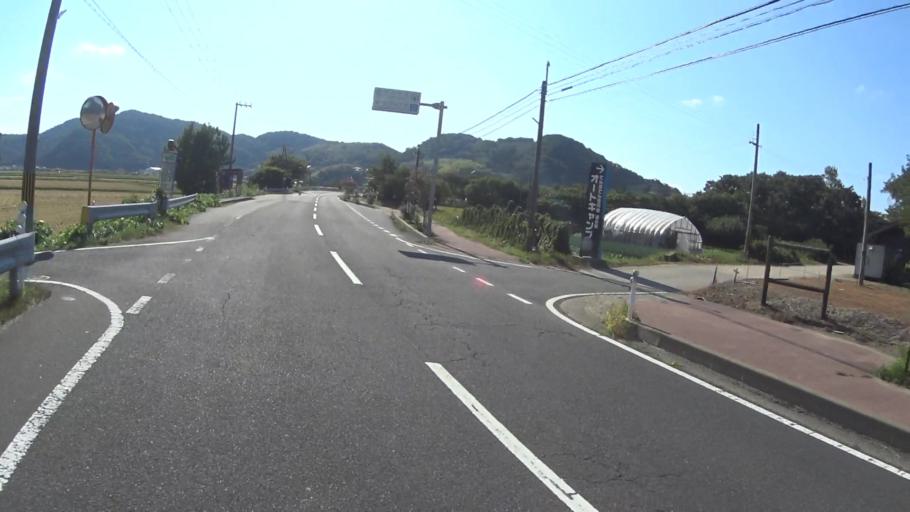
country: JP
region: Kyoto
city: Miyazu
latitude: 35.7387
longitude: 135.1076
